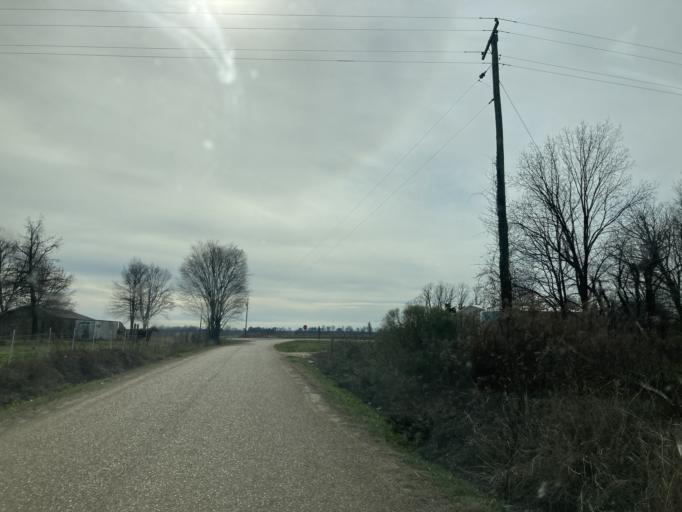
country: US
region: Mississippi
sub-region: Humphreys County
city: Belzoni
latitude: 33.1393
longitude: -90.6068
